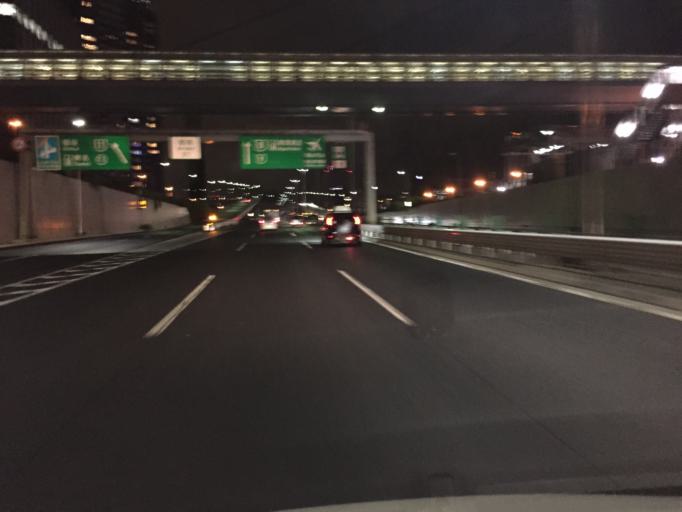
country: JP
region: Tokyo
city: Tokyo
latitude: 35.6280
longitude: 139.7784
